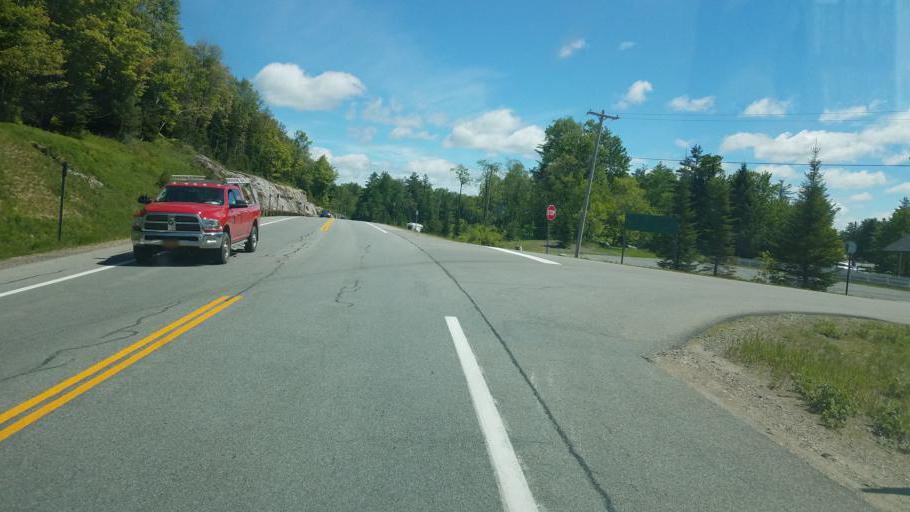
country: US
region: New York
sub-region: Oneida County
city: Boonville
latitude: 43.6988
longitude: -75.0064
